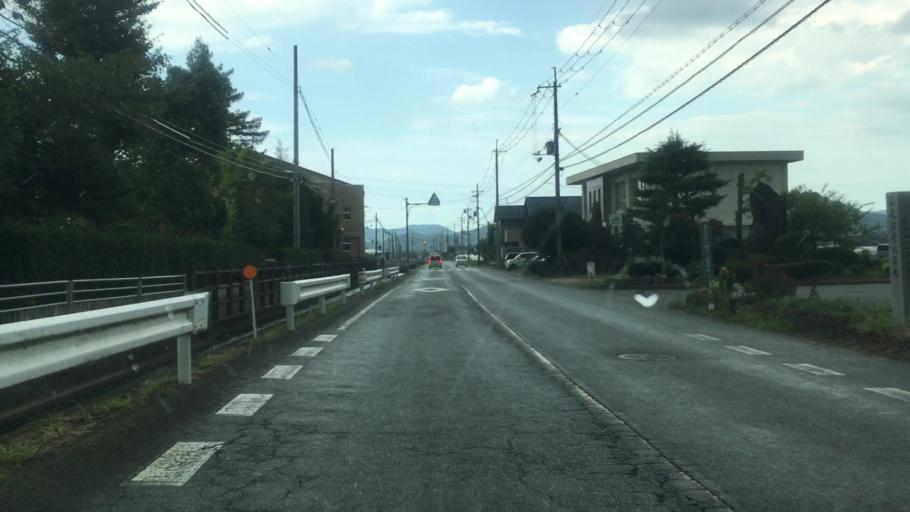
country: JP
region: Hyogo
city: Toyooka
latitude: 35.5015
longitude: 134.8200
